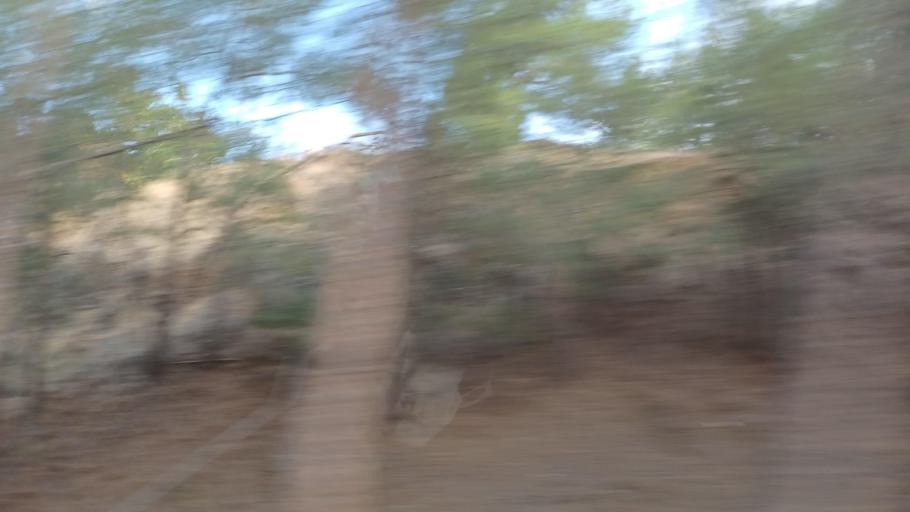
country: CY
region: Lefkosia
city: Kakopetria
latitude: 35.0542
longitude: 32.9105
